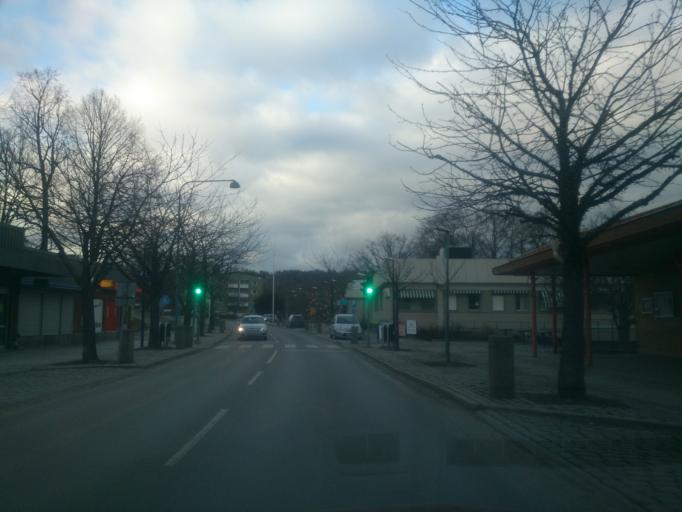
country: SE
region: OEstergoetland
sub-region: Norrkopings Kommun
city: Jursla
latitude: 58.6649
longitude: 16.1815
